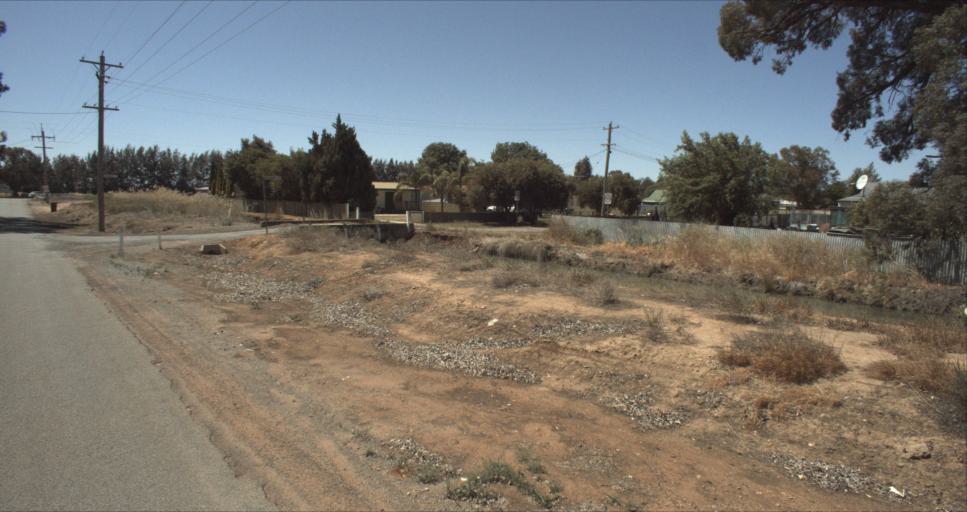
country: AU
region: New South Wales
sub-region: Leeton
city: Leeton
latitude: -34.5237
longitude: 146.3304
